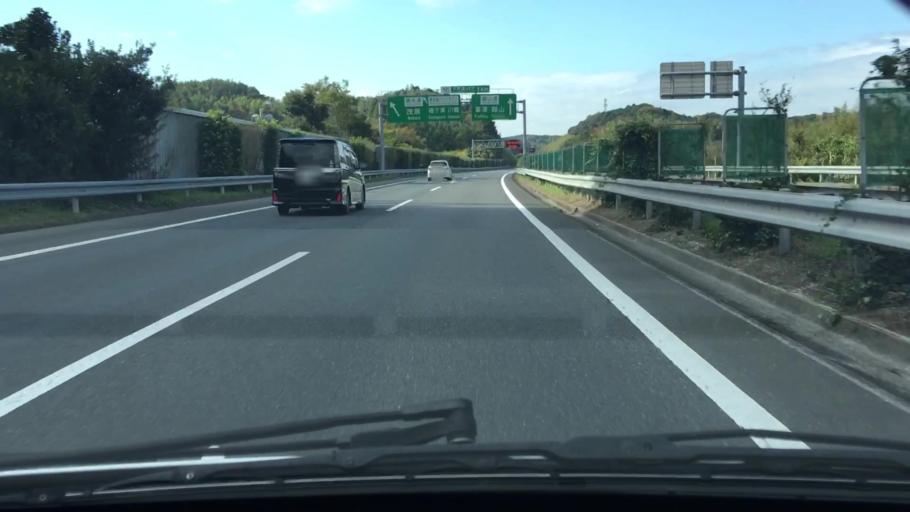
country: JP
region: Chiba
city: Kisarazu
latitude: 35.3840
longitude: 139.9941
